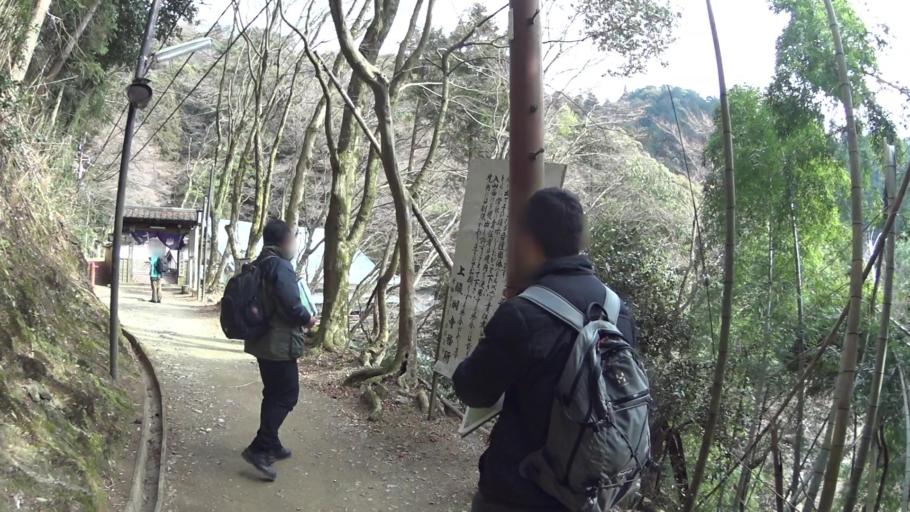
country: JP
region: Kyoto
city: Uji
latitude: 34.9452
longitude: 135.8373
